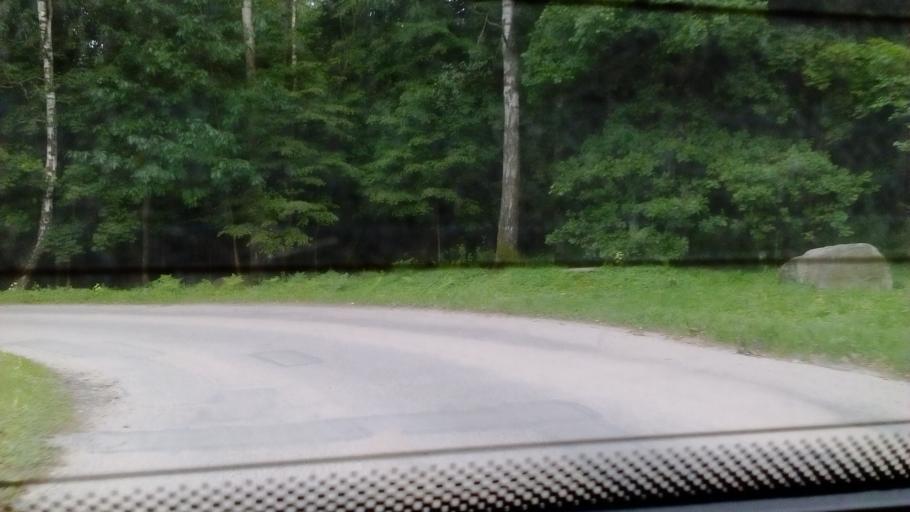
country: LT
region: Alytaus apskritis
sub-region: Alytus
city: Alytus
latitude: 54.3943
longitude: 24.0704
